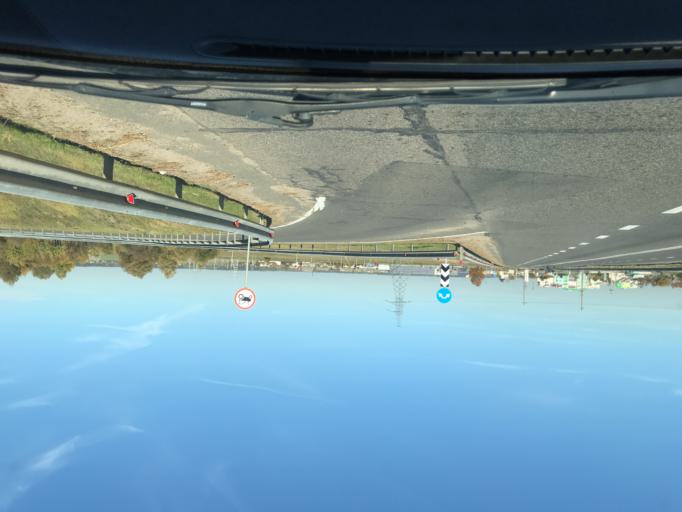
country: BY
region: Brest
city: Ivatsevichy
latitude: 52.7002
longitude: 25.3624
